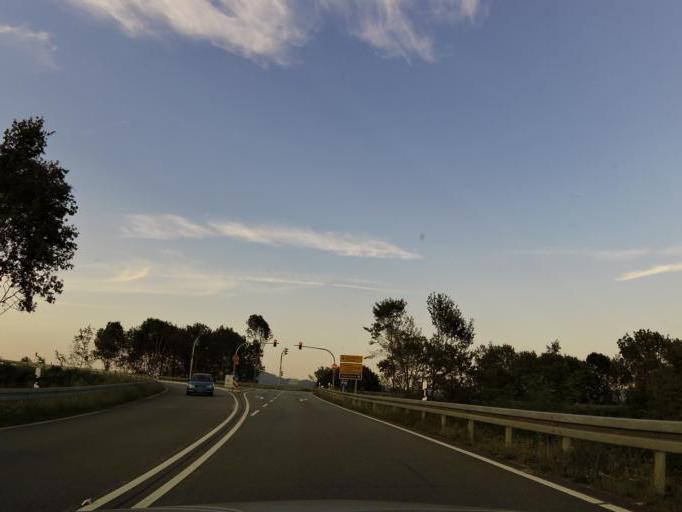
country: DE
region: Hesse
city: Lorsch
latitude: 49.6634
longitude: 8.5704
